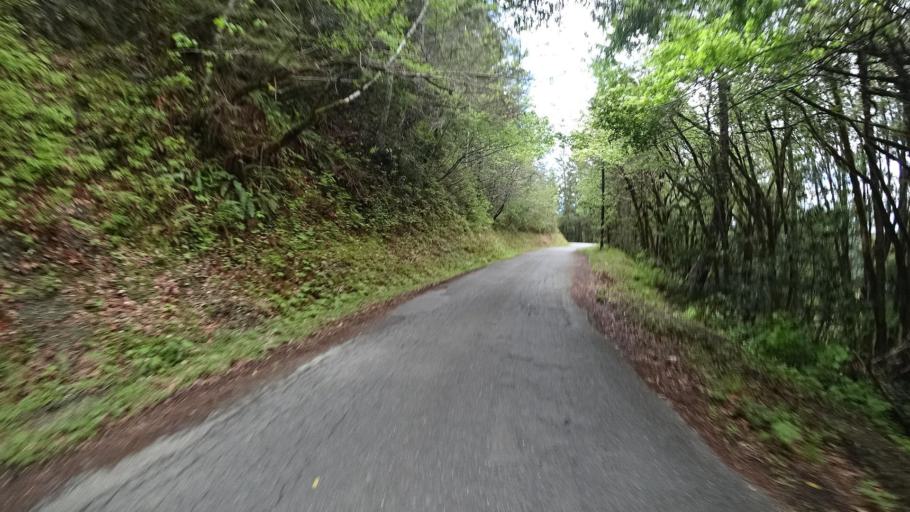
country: US
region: California
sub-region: Humboldt County
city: Blue Lake
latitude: 40.7602
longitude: -123.9037
